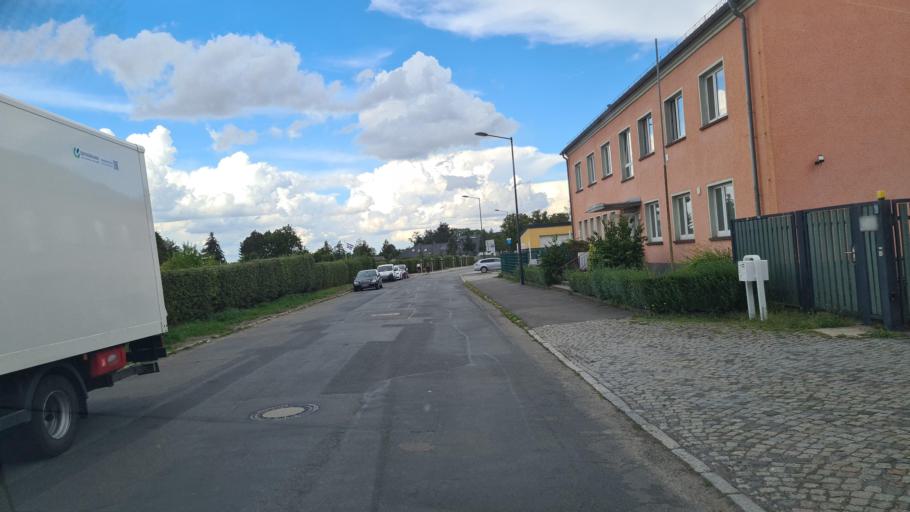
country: DE
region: Saxony
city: Taucha
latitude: 51.3803
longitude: 12.4813
